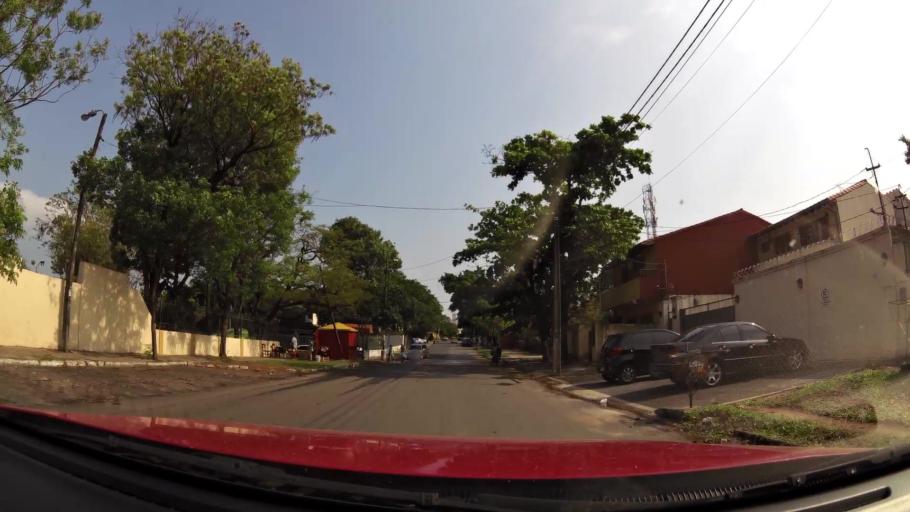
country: PY
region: Presidente Hayes
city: Nanawa
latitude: -25.2939
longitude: -57.6662
